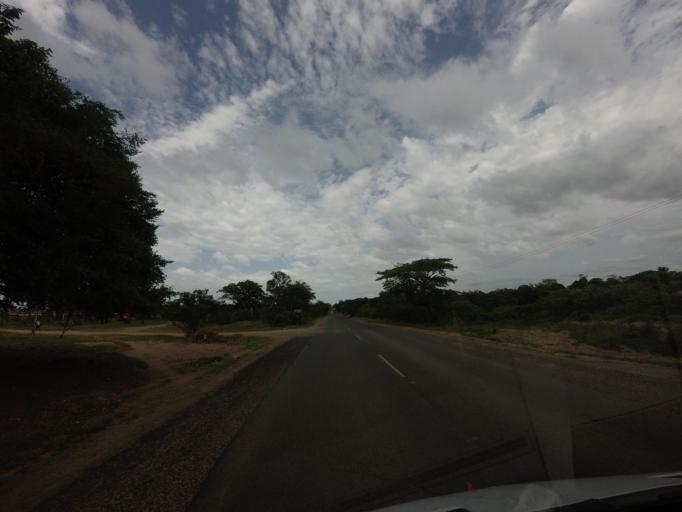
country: ZA
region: KwaZulu-Natal
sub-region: uMkhanyakude District Municipality
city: Mtubatuba
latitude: -28.3800
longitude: 32.3639
